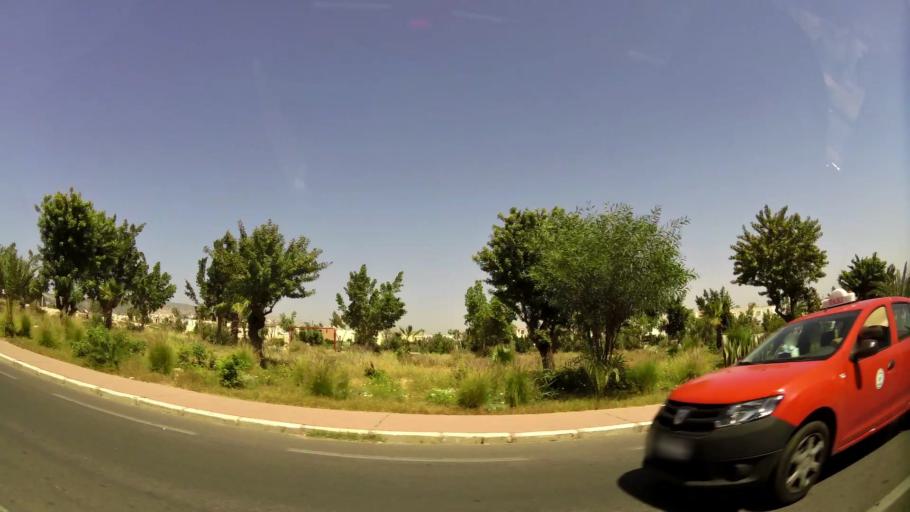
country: MA
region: Souss-Massa-Draa
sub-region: Agadir-Ida-ou-Tnan
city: Agadir
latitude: 30.4305
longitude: -9.5932
